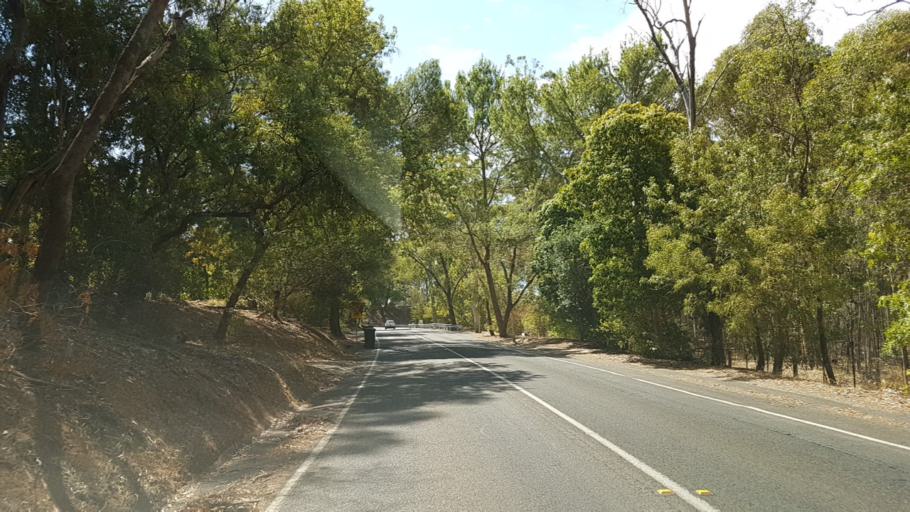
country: AU
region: South Australia
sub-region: Mitcham
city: Belair
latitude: -35.0001
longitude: 138.6326
